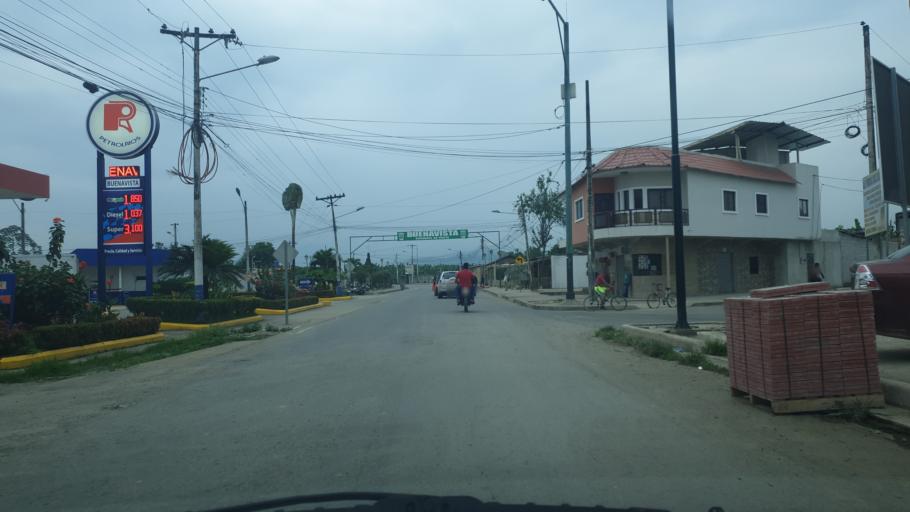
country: EC
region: El Oro
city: Pasaje
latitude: -3.3624
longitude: -79.8419
